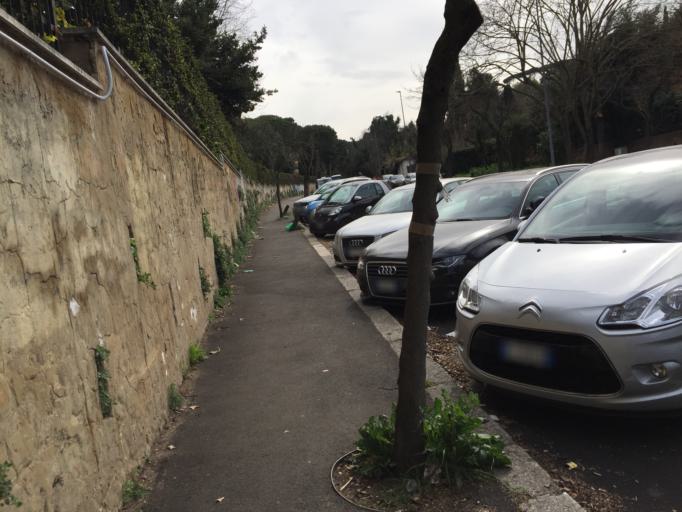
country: VA
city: Vatican City
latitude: 41.8926
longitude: 12.4586
